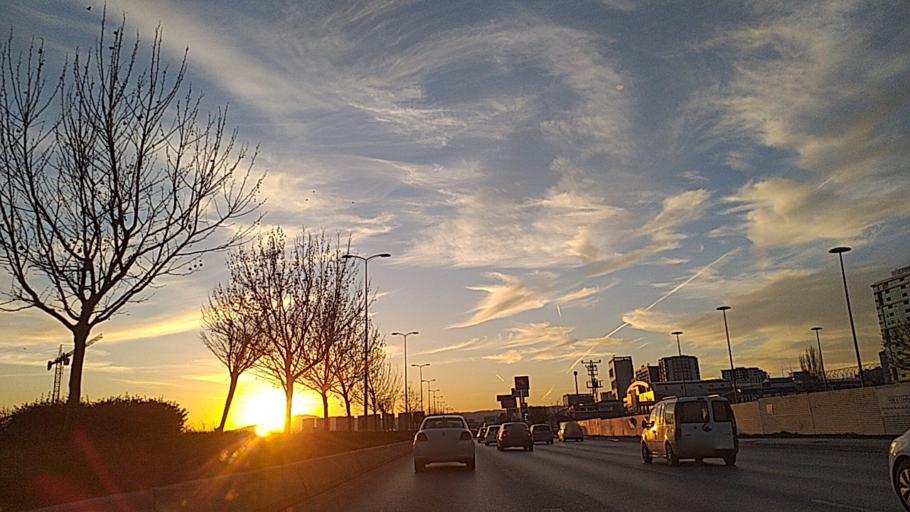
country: TR
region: Ankara
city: Etimesgut
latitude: 39.9637
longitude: 32.6491
